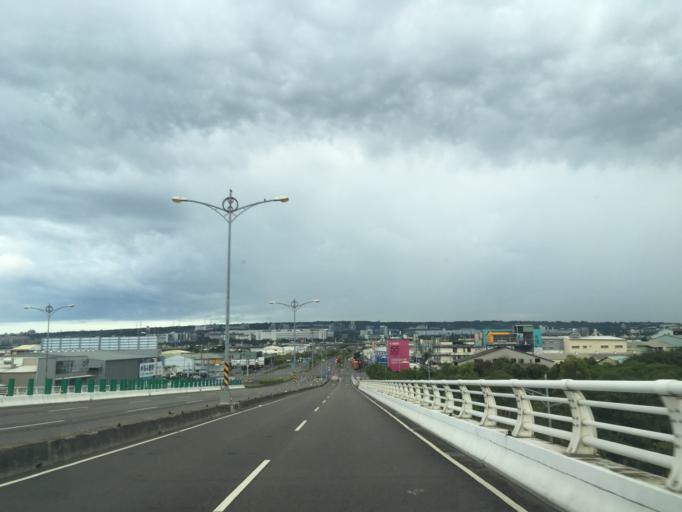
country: TW
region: Taiwan
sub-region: Taichung City
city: Taichung
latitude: 24.2011
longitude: 120.6468
